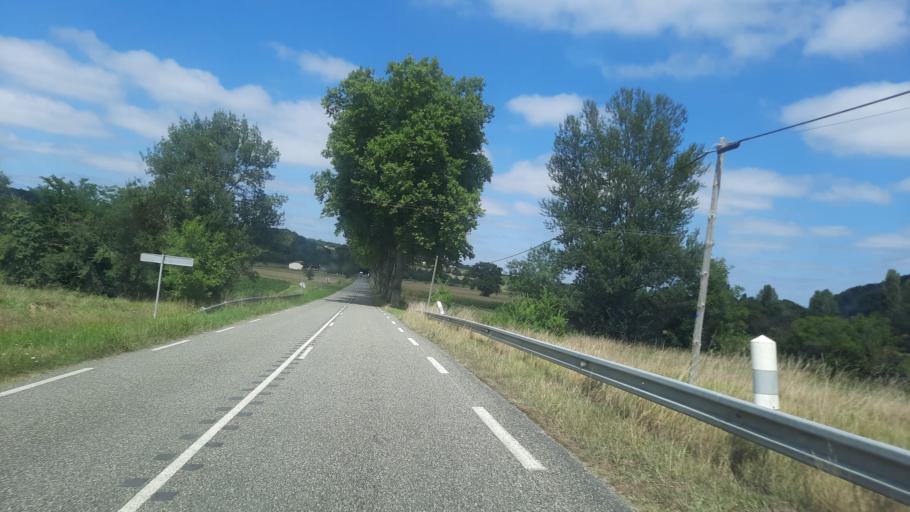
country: FR
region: Midi-Pyrenees
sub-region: Departement de la Haute-Garonne
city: Boulogne-sur-Gesse
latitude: 43.3704
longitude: 0.7529
